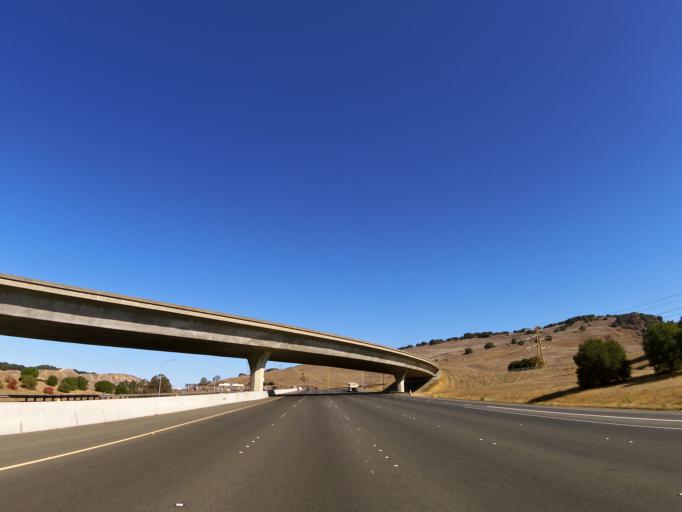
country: US
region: California
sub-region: Solano County
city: Vallejo
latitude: 38.1404
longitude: -122.2192
